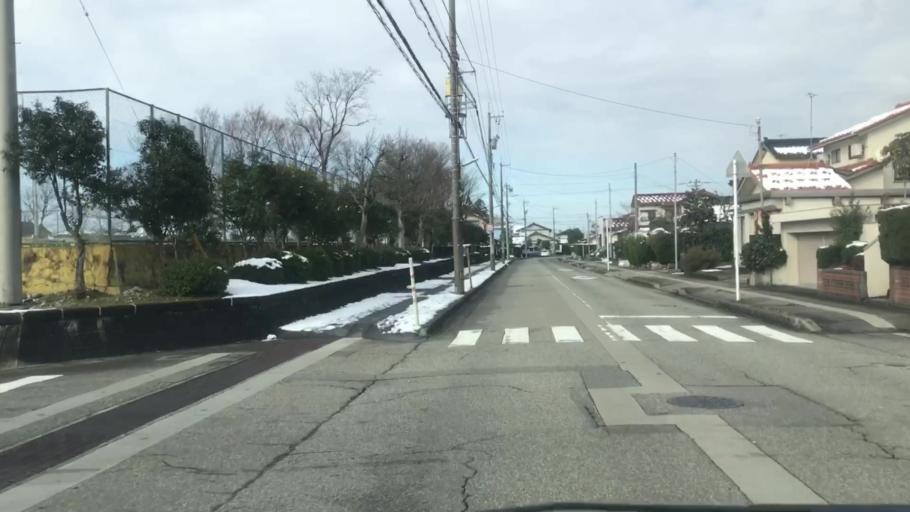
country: JP
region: Toyama
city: Toyama-shi
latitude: 36.6155
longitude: 137.2557
